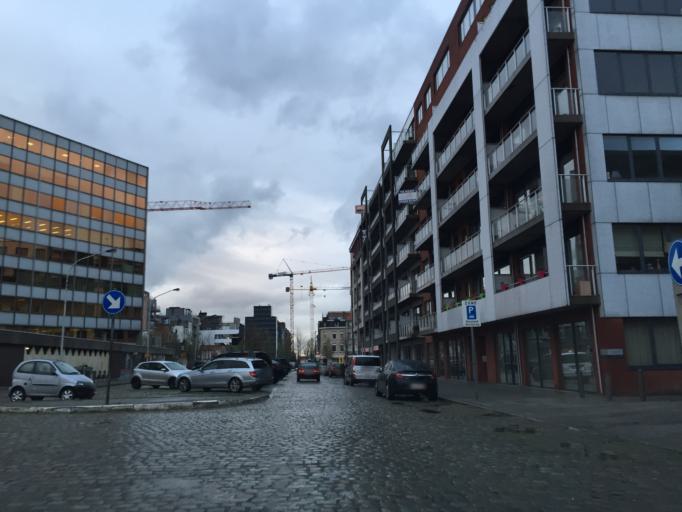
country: BE
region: Flanders
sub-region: Provincie Antwerpen
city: Antwerpen
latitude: 51.2301
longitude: 4.4040
